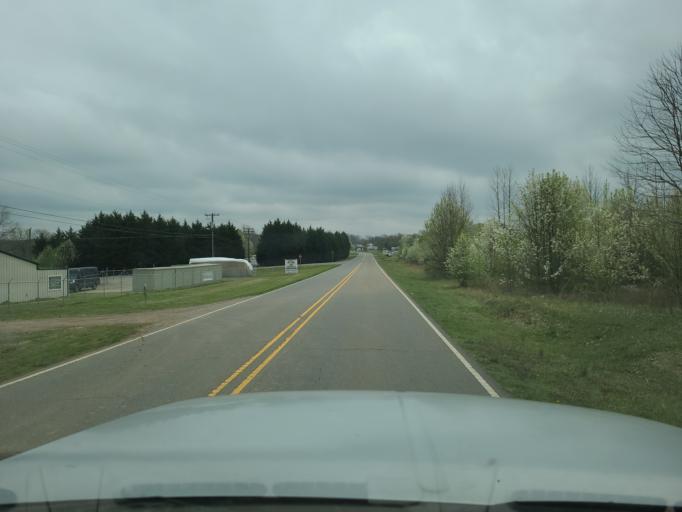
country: US
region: North Carolina
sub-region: Cleveland County
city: Shelby
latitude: 35.3730
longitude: -81.5994
